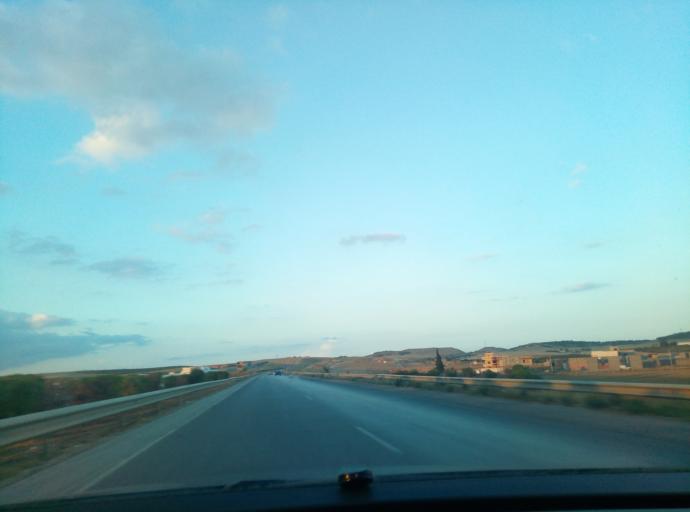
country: TN
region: Manouba
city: Manouba
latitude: 36.7468
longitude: 10.0372
